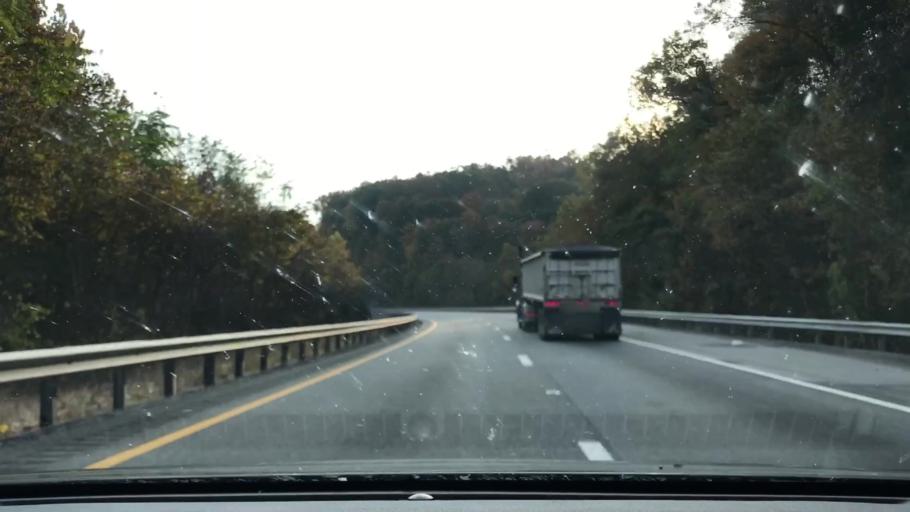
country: US
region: Tennessee
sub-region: Putnam County
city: Algood
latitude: 36.1422
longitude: -85.3929
